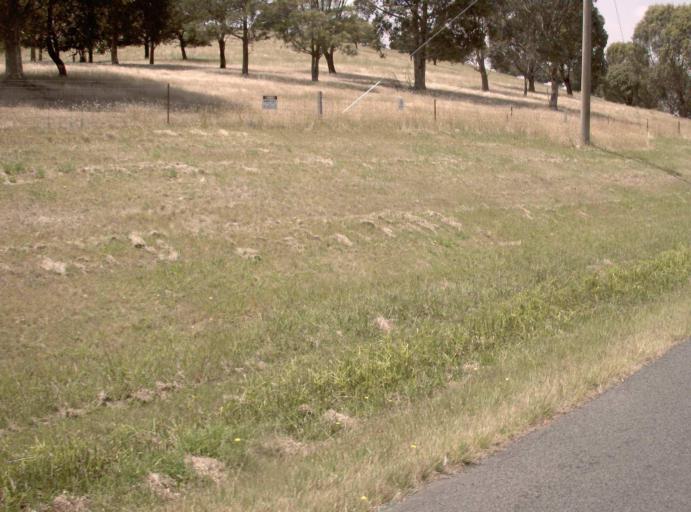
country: AU
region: Victoria
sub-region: Latrobe
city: Traralgon
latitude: -38.2403
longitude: 146.5442
